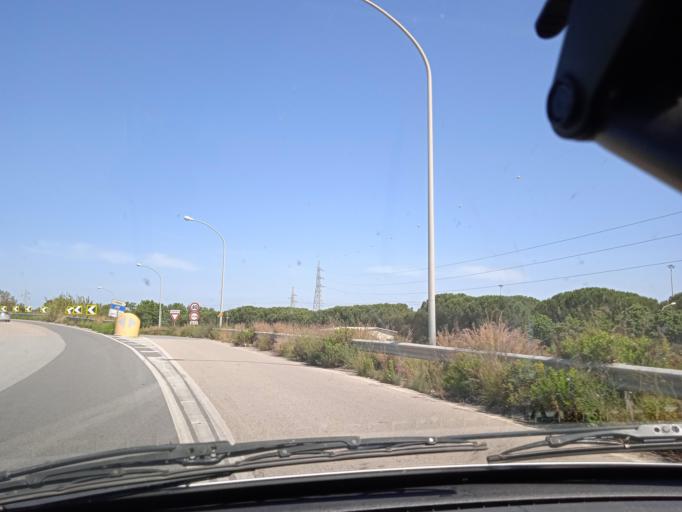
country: IT
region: Sicily
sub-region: Messina
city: Milazzo
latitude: 38.1966
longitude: 15.2542
